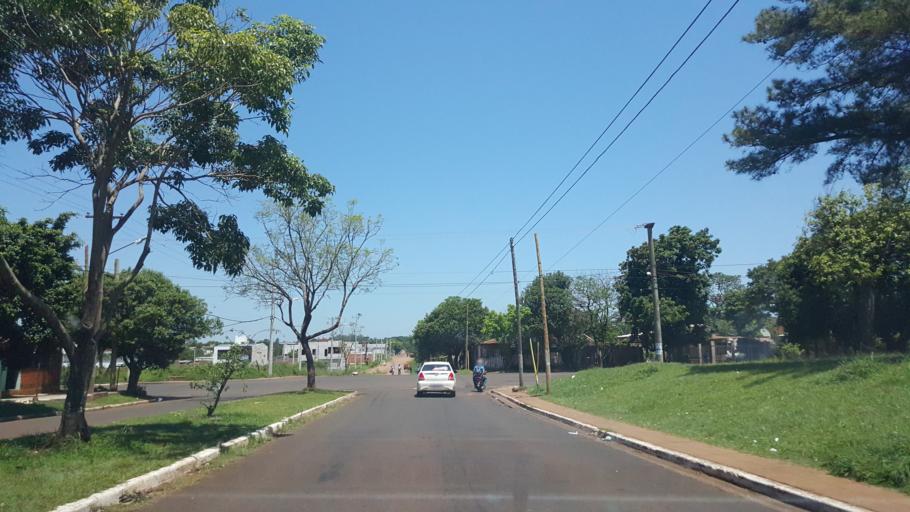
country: AR
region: Misiones
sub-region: Departamento de Capital
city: Posadas
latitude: -27.3809
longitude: -55.9261
